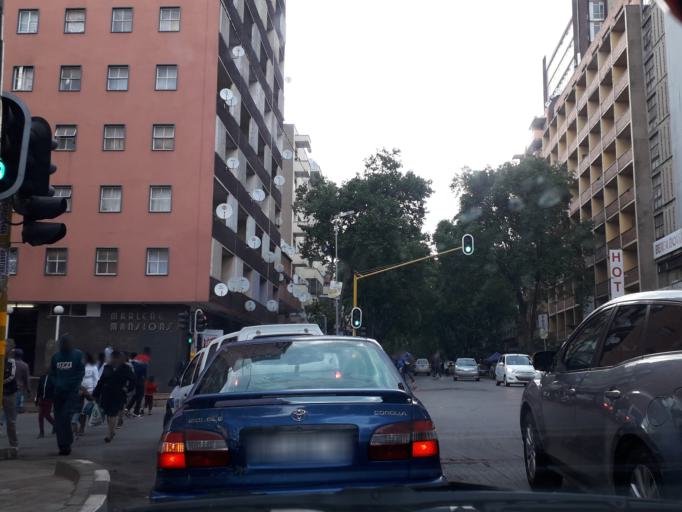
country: ZA
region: Gauteng
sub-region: City of Johannesburg Metropolitan Municipality
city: Johannesburg
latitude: -26.1883
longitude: 28.0547
